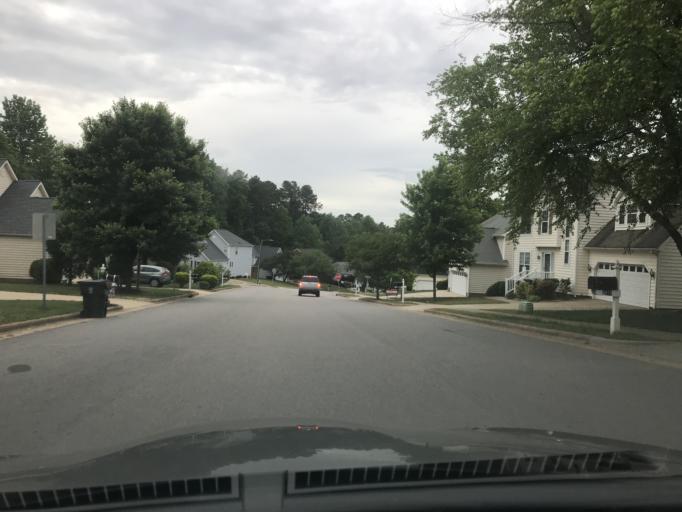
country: US
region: North Carolina
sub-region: Wake County
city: West Raleigh
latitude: 35.8858
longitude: -78.5953
